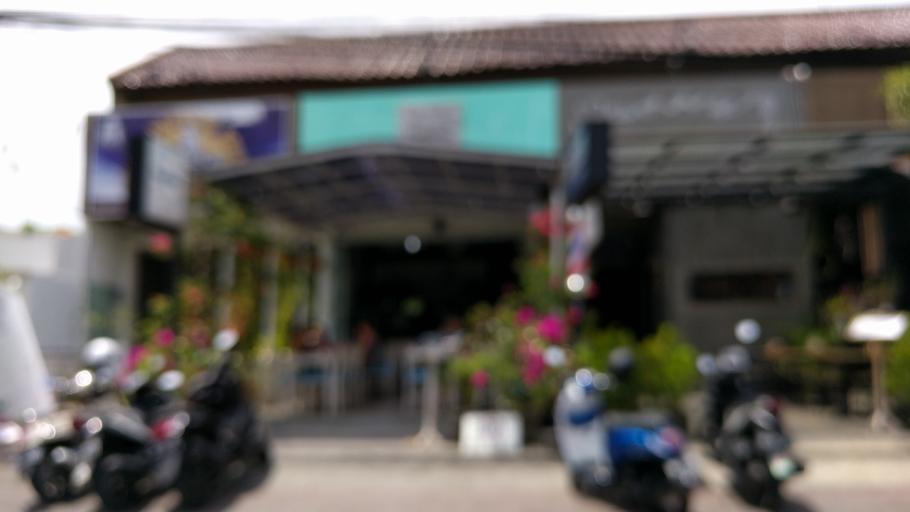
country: ID
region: Bali
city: Kuta
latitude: -8.6718
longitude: 115.1623
